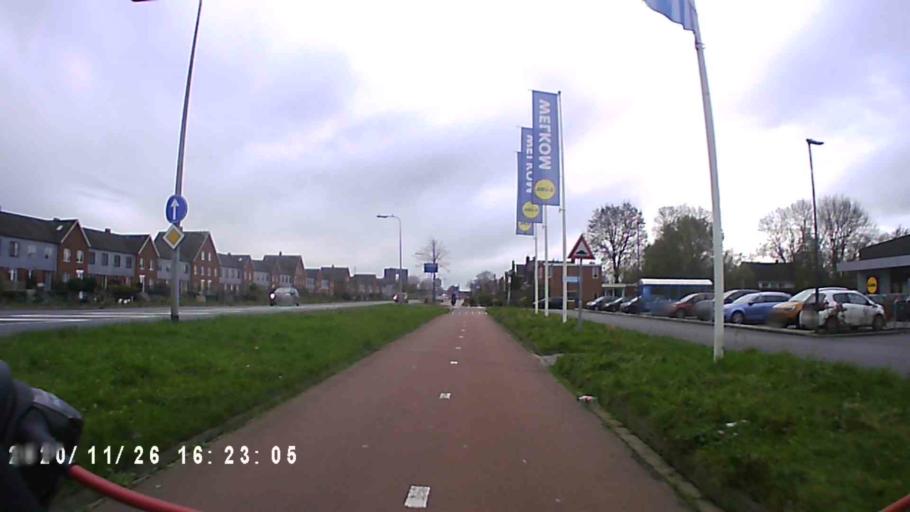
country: NL
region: Groningen
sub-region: Gemeente Groningen
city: Oosterpark
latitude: 53.2311
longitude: 6.6184
